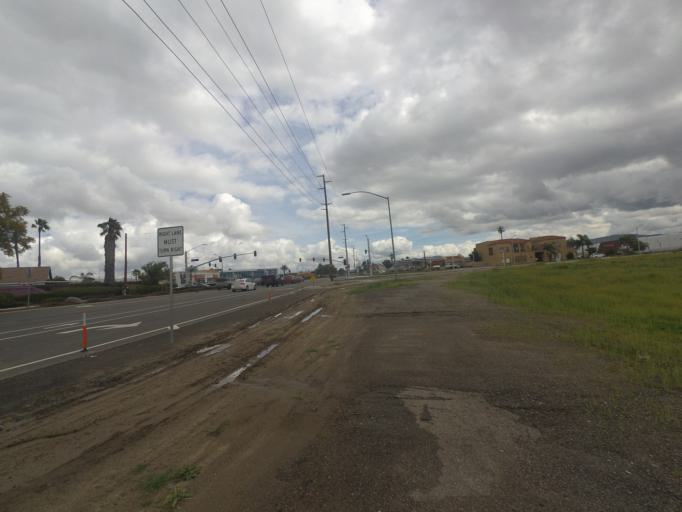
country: US
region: California
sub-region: Riverside County
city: March Air Force Base
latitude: 33.9170
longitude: -117.2534
